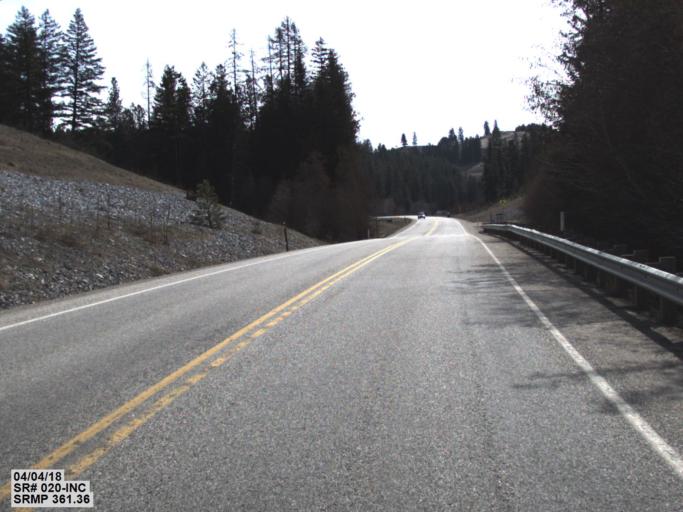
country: US
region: Washington
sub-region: Stevens County
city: Colville
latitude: 48.5145
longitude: -117.7804
